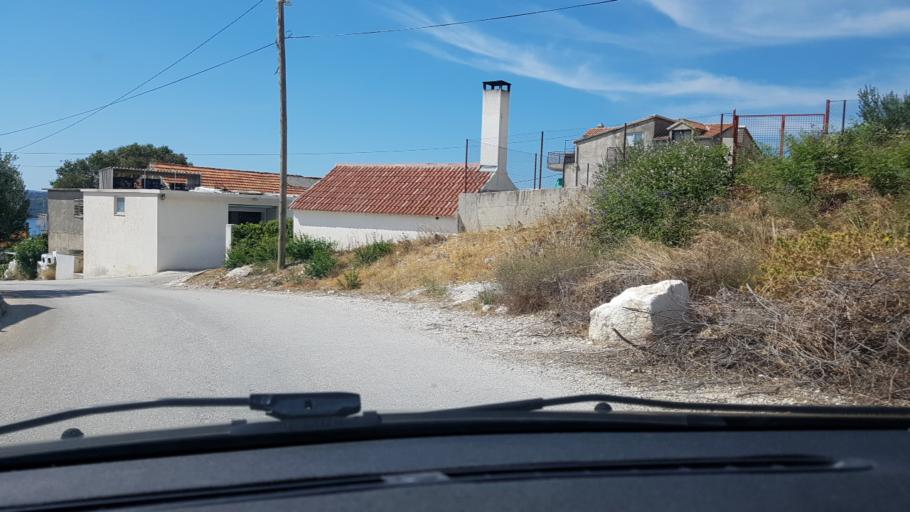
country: HR
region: Splitsko-Dalmatinska
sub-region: Grad Trogir
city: Trogir
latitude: 43.5244
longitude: 16.2265
